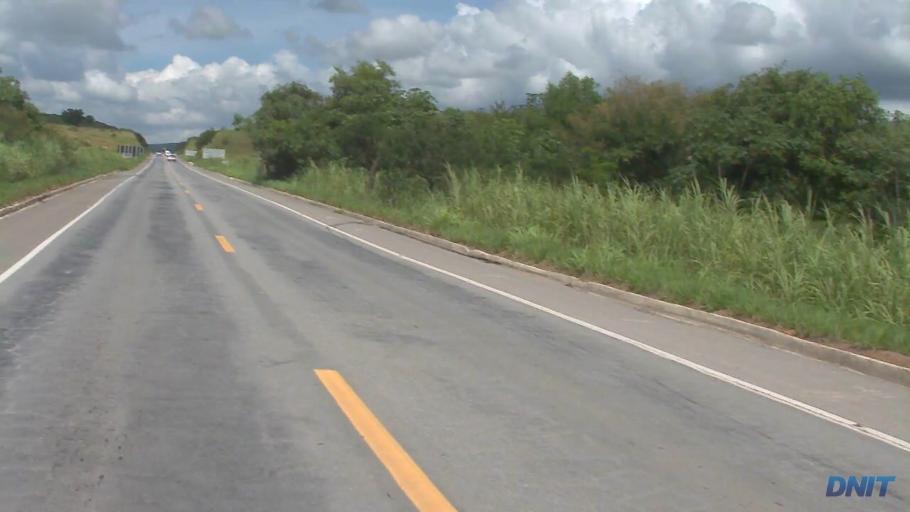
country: BR
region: Minas Gerais
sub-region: Governador Valadares
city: Governador Valadares
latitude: -18.9944
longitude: -42.1186
